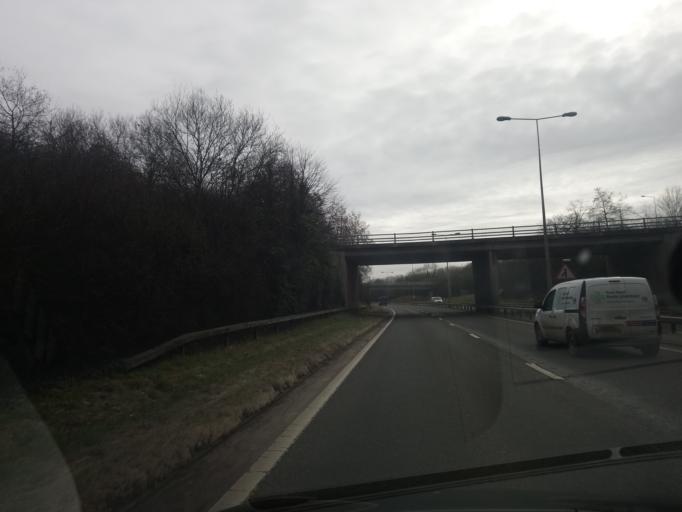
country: GB
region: England
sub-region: Telford and Wrekin
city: Oakengates
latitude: 52.7046
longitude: -2.4588
